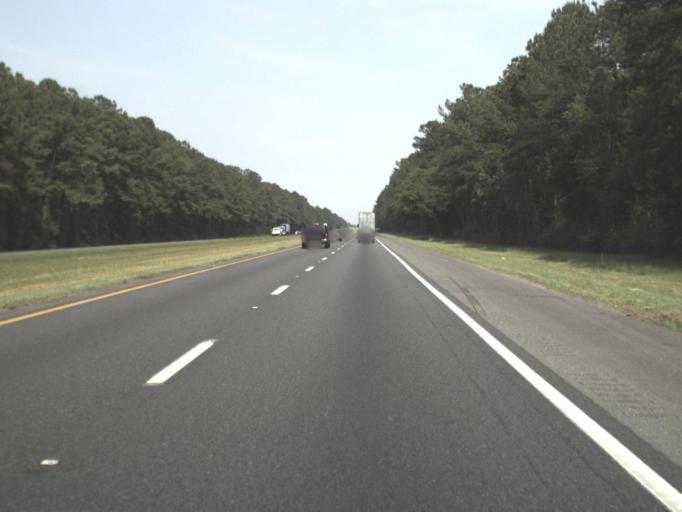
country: US
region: Florida
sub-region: Baker County
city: Macclenny
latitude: 30.2608
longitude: -82.1521
